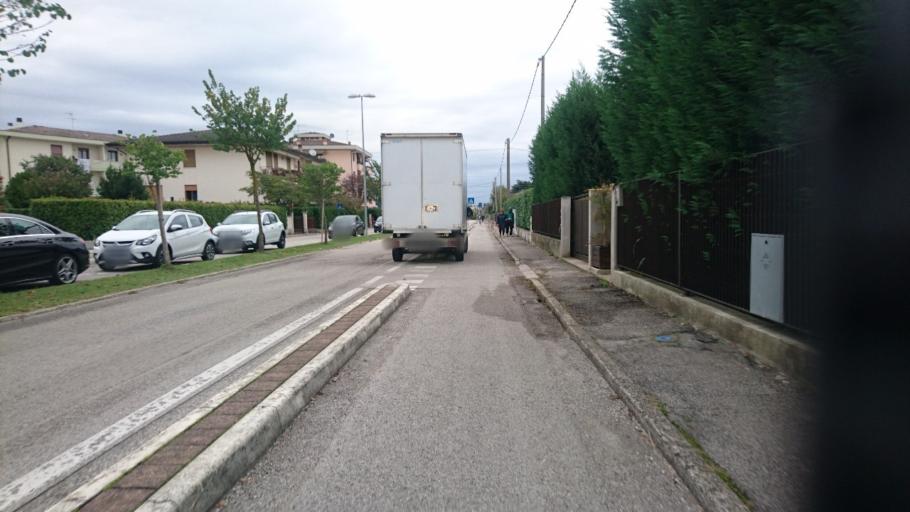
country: IT
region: Veneto
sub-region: Provincia di Vicenza
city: Creazzo
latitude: 45.5299
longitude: 11.4786
